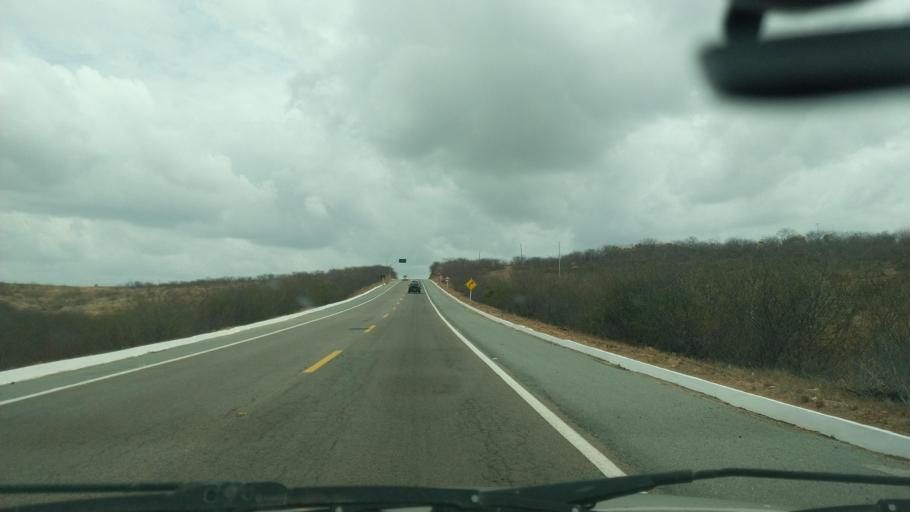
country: BR
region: Rio Grande do Norte
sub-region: Currais Novos
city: Currais Novos
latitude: -6.2182
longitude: -36.4257
